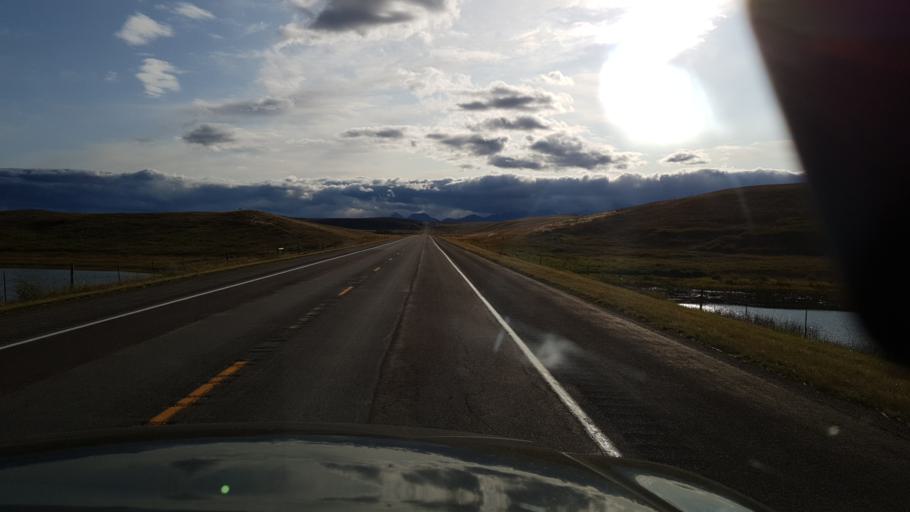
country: US
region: Montana
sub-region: Glacier County
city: South Browning
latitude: 48.5350
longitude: -113.0466
